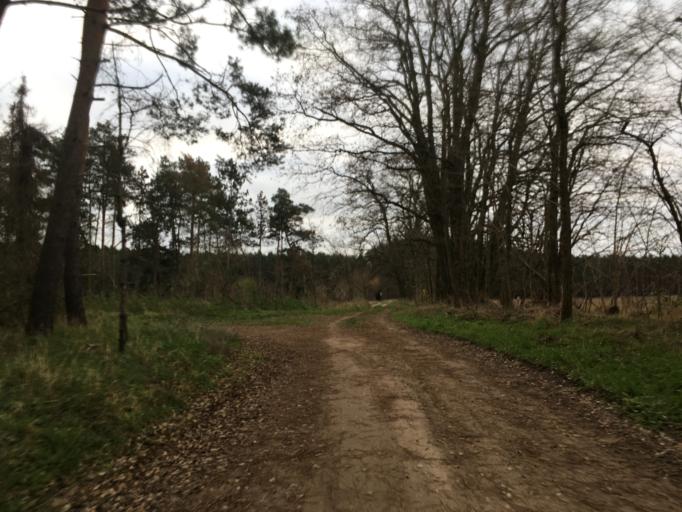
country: DE
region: Brandenburg
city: Neuhardenberg
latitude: 52.5839
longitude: 14.2441
